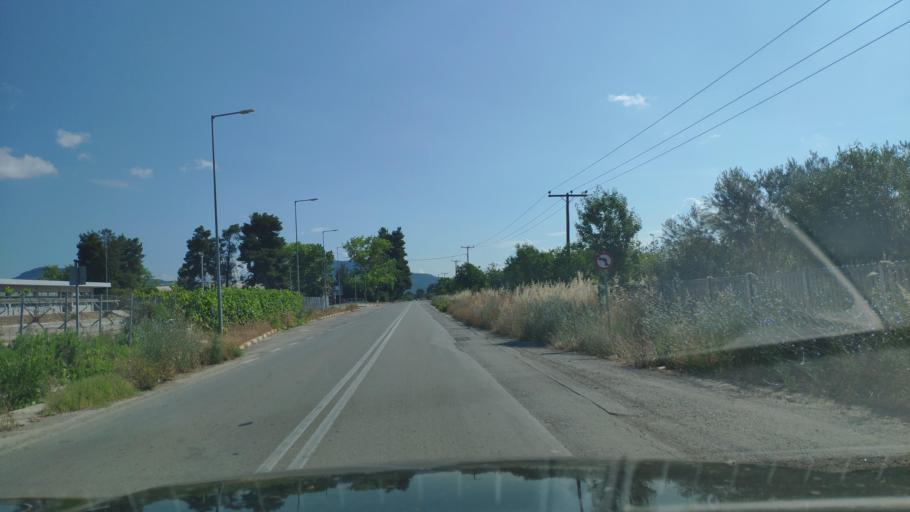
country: GR
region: Central Greece
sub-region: Nomos Voiotias
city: Arma
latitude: 38.3823
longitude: 23.4967
